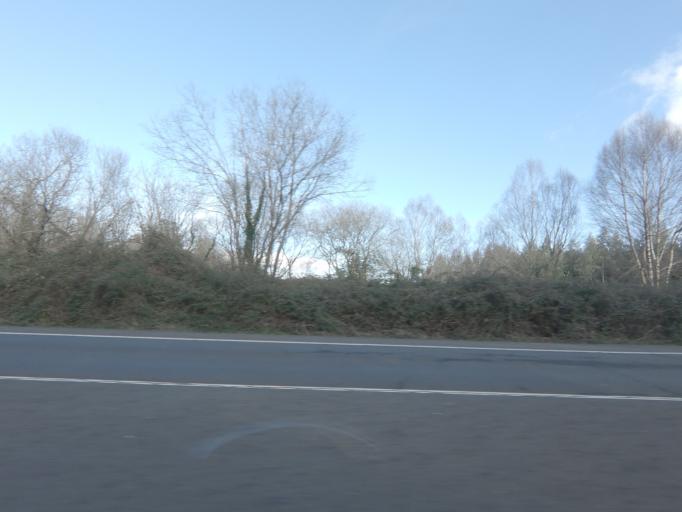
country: ES
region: Galicia
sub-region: Provincia da Coruna
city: Ribeira
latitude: 42.7133
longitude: -8.3592
